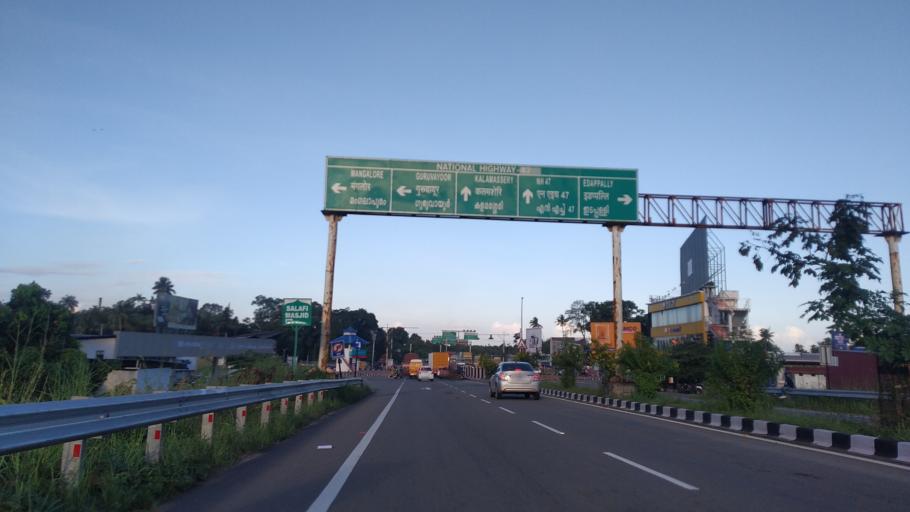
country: IN
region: Kerala
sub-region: Ernakulam
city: Elur
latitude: 10.0610
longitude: 76.2875
